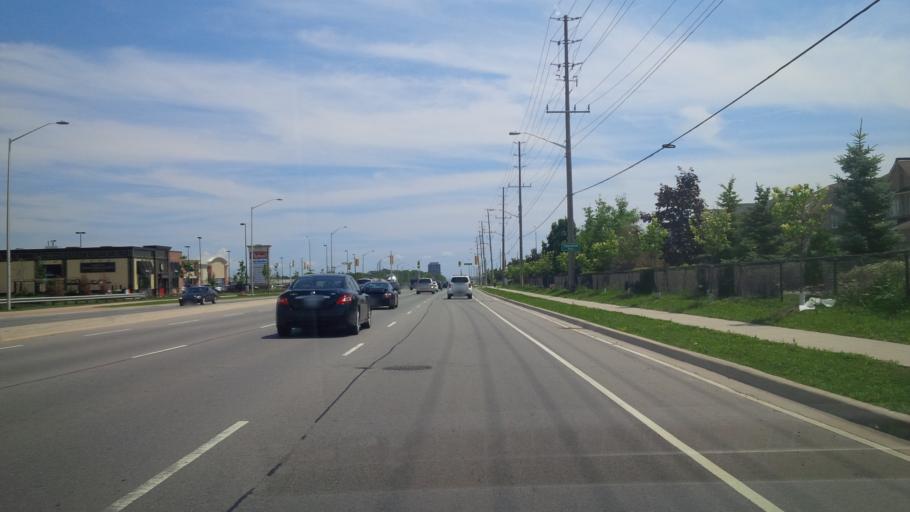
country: CA
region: Ontario
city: Burlington
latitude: 43.4044
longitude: -79.8052
